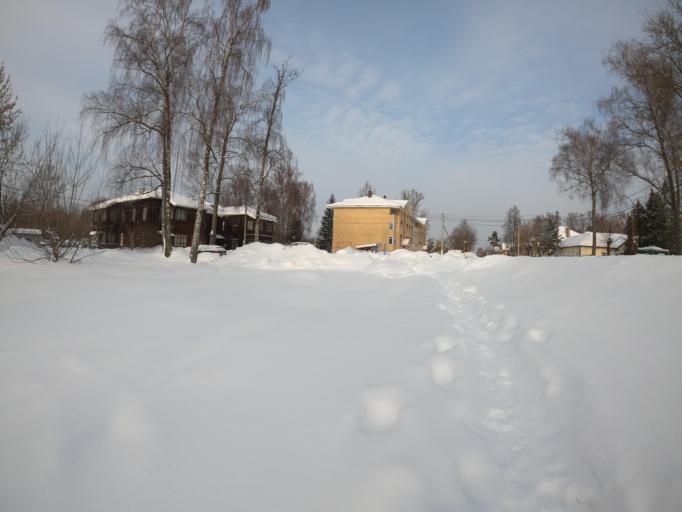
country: RU
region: Moskovskaya
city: Elektrogorsk
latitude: 55.8930
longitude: 38.7699
